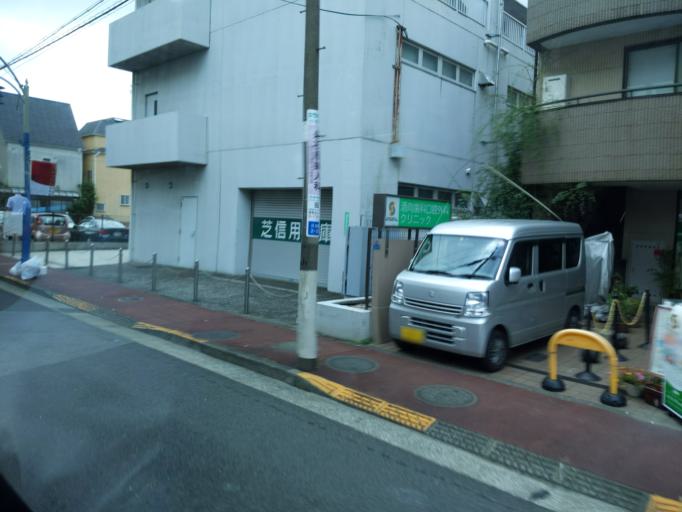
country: JP
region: Kanagawa
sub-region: Kawasaki-shi
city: Kawasaki
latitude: 35.5817
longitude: 139.6972
